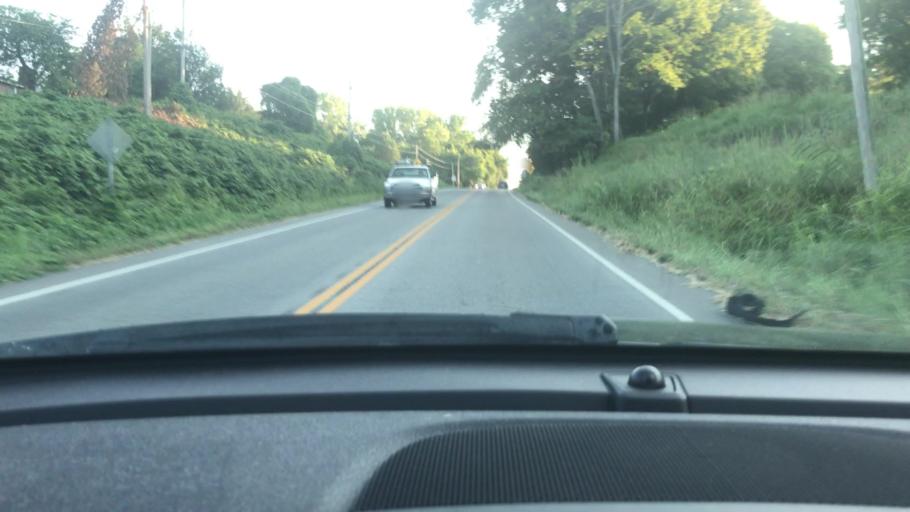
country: US
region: Tennessee
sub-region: Dickson County
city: Charlotte
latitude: 36.1733
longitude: -87.3444
